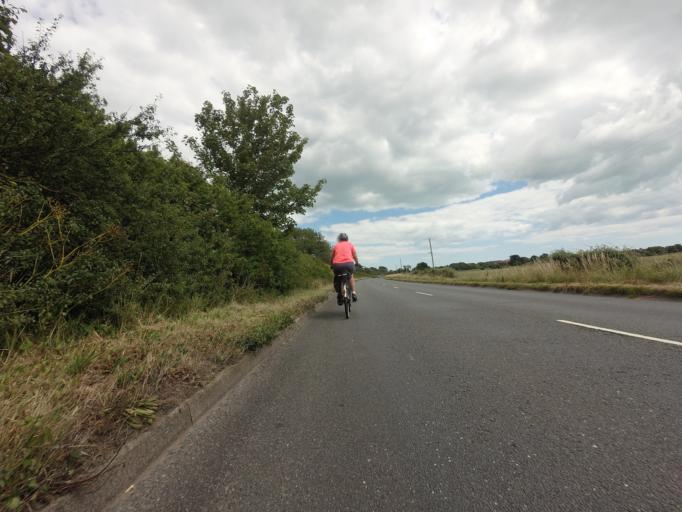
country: GB
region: England
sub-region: East Sussex
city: Pevensey
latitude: 50.8170
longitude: 0.3457
